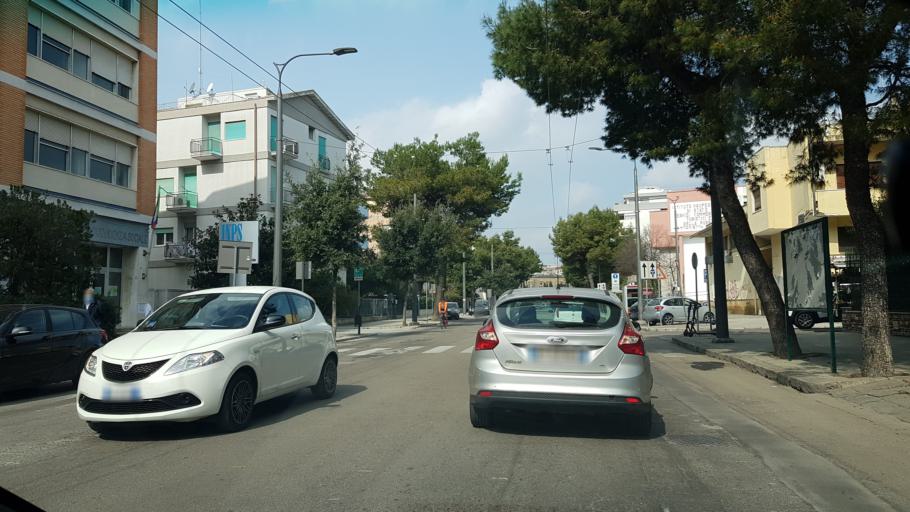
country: IT
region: Apulia
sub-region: Provincia di Lecce
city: Lecce
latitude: 40.3438
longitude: 18.1727
